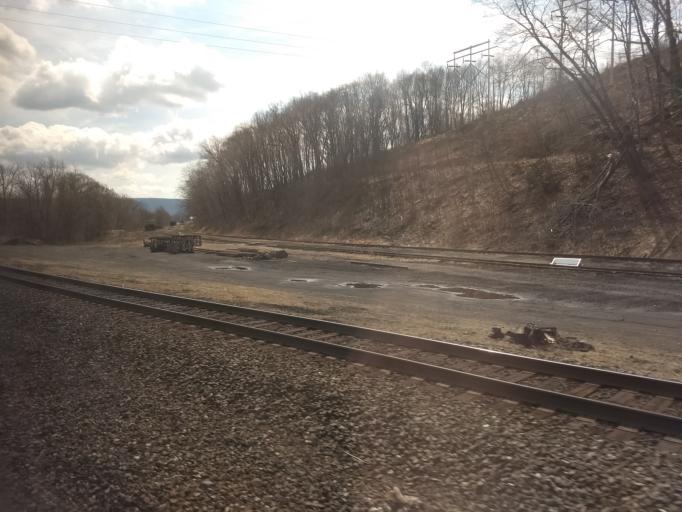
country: US
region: Pennsylvania
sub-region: Huntingdon County
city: Mount Union
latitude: 40.3906
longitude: -77.8924
